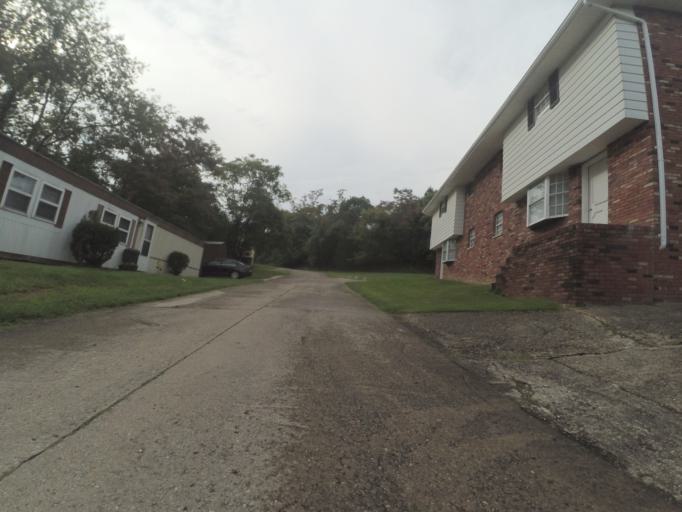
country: US
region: West Virginia
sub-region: Cabell County
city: Huntington
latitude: 38.3850
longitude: -82.4250
